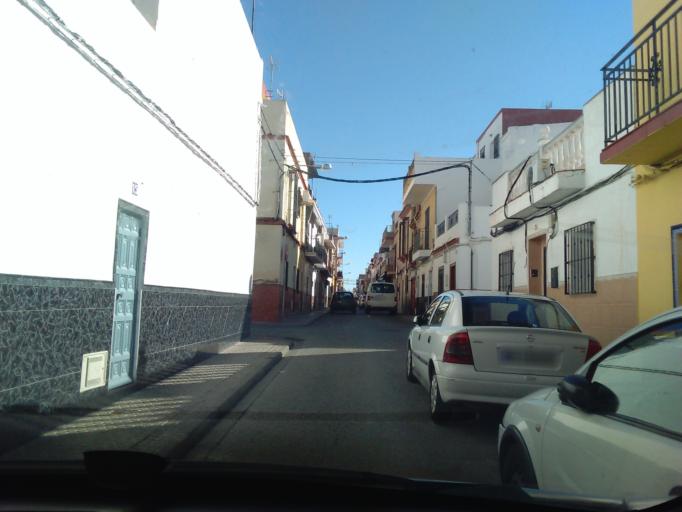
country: ES
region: Andalusia
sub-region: Provincia de Sevilla
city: Sevilla
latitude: 37.3852
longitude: -5.9088
